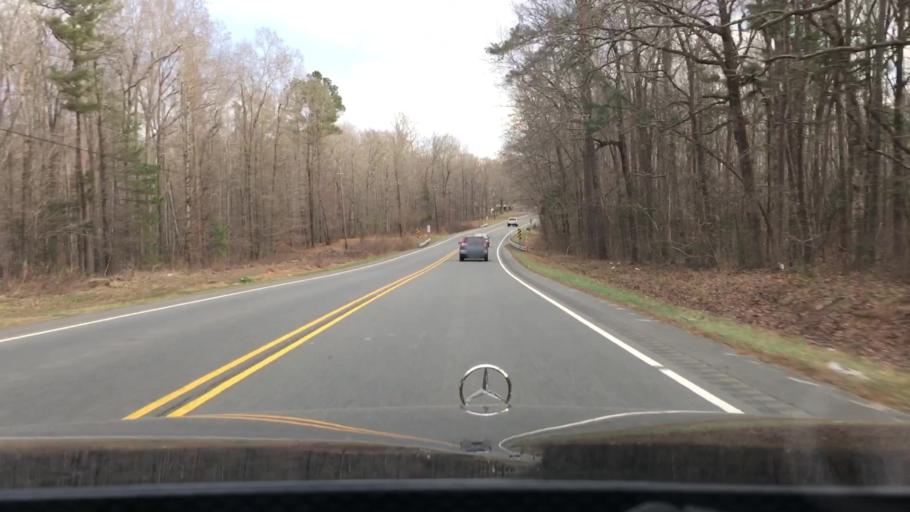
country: US
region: North Carolina
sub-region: Orange County
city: Hillsborough
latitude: 36.2025
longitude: -79.1465
